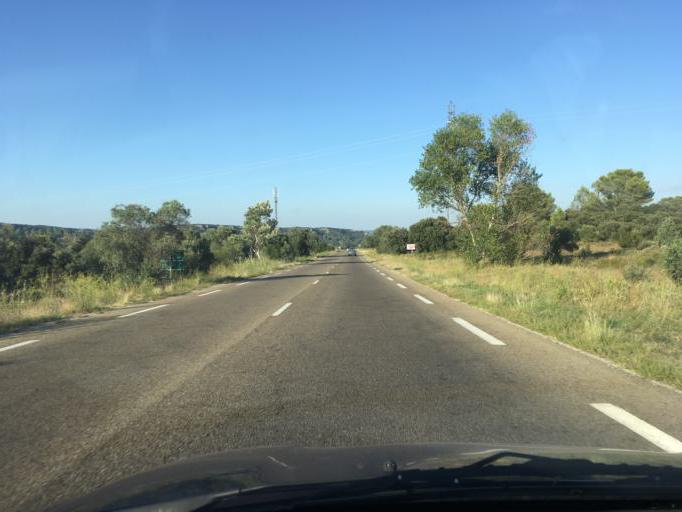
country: FR
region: Languedoc-Roussillon
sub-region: Departement du Gard
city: Ledenon
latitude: 43.9156
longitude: 4.5298
